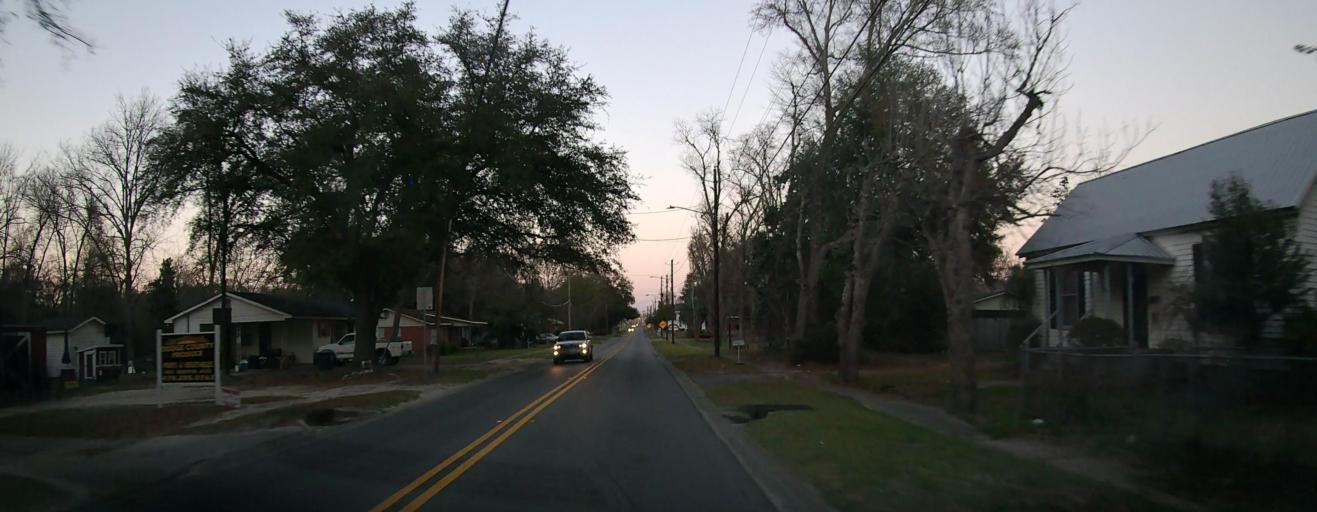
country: US
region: Georgia
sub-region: Dodge County
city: Eastman
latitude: 32.1886
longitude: -83.1775
